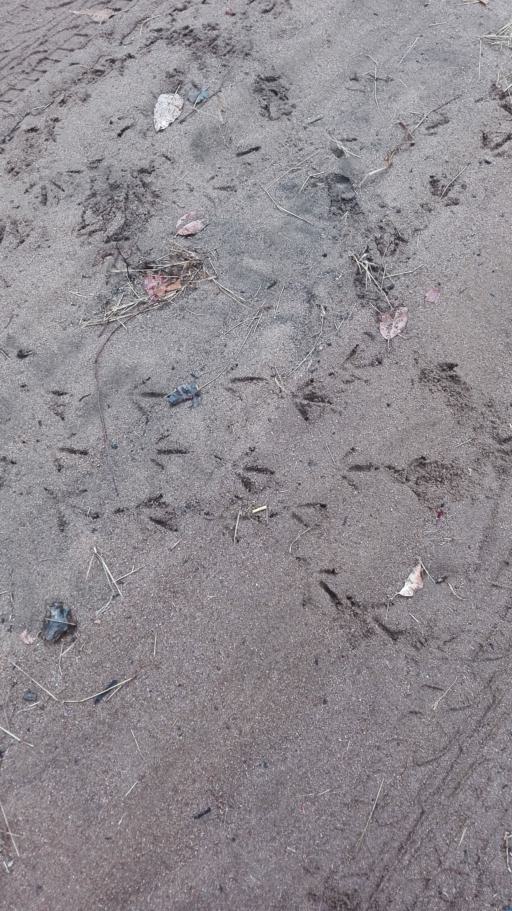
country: MZ
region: Nampula
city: Mutuali
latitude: -15.4666
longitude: 36.9781
